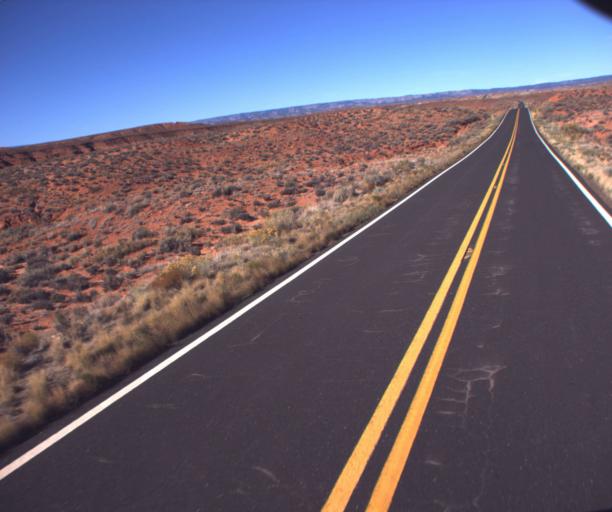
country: US
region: Arizona
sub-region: Coconino County
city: Page
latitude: 36.6866
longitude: -111.8657
